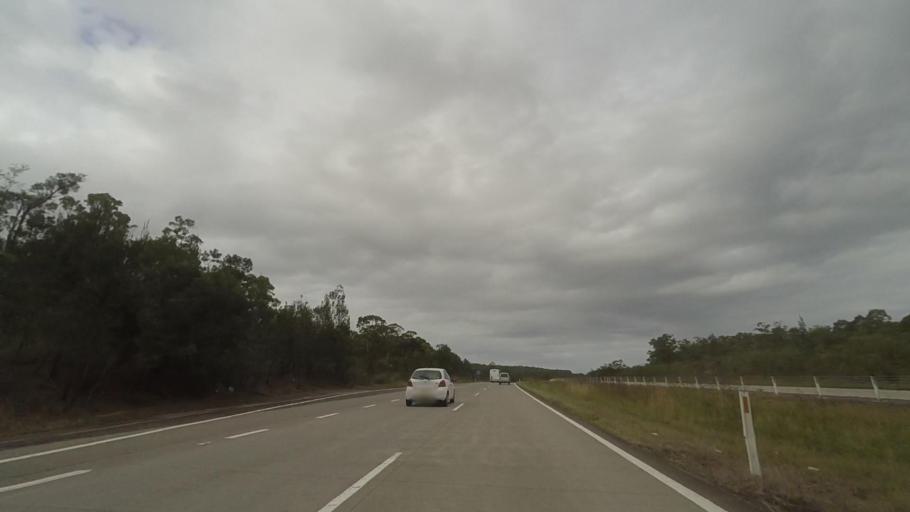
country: AU
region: New South Wales
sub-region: Port Stephens Shire
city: Port Stephens
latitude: -32.6268
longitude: 152.0542
